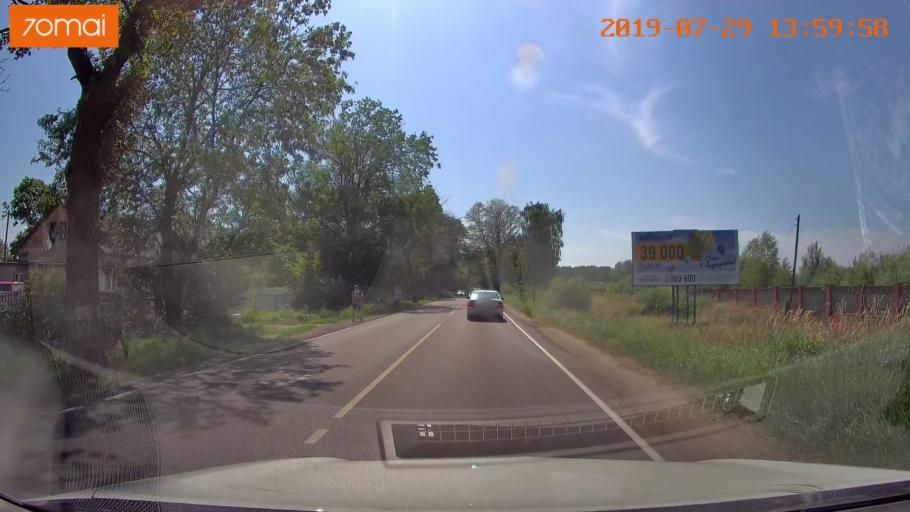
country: RU
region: Kaliningrad
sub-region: Gorod Kaliningrad
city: Baltiysk
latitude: 54.6820
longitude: 19.9303
